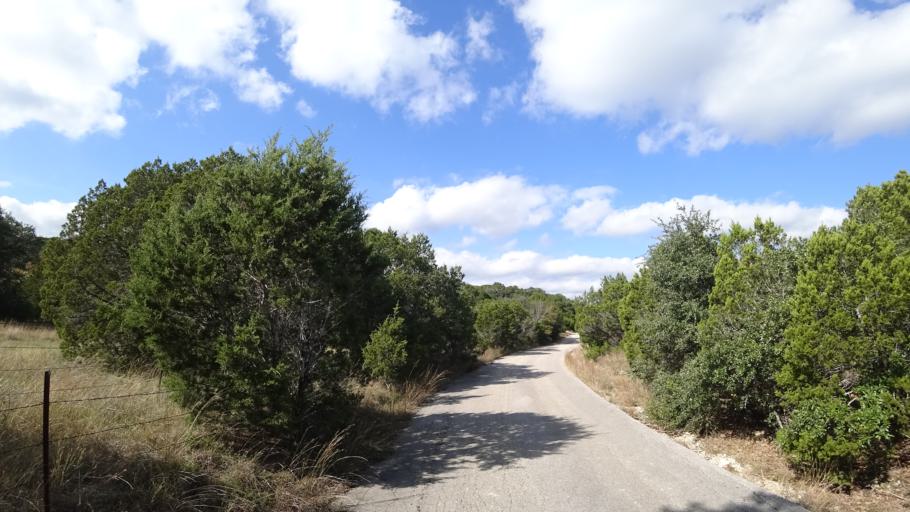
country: US
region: Texas
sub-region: Travis County
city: Bee Cave
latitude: 30.2586
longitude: -97.9431
